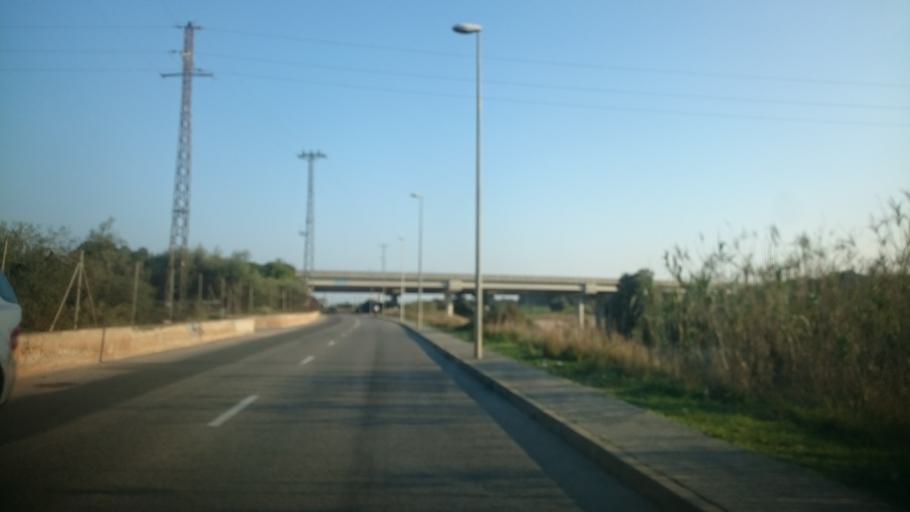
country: ES
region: Catalonia
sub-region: Provincia de Barcelona
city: Cubelles
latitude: 41.2149
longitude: 1.6637
